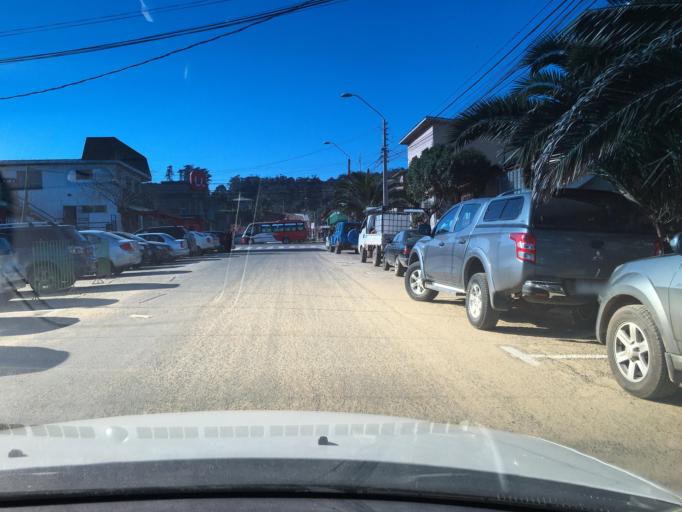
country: CL
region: Valparaiso
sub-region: San Antonio Province
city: El Tabo
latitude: -33.4564
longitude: -71.6657
